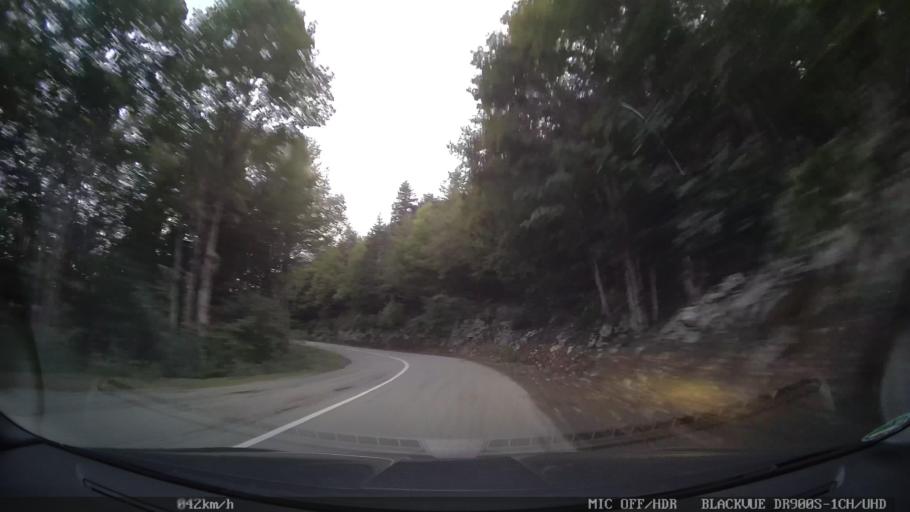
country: HR
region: Primorsko-Goranska
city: Novi Vinodolski
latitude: 45.1955
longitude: 14.8926
